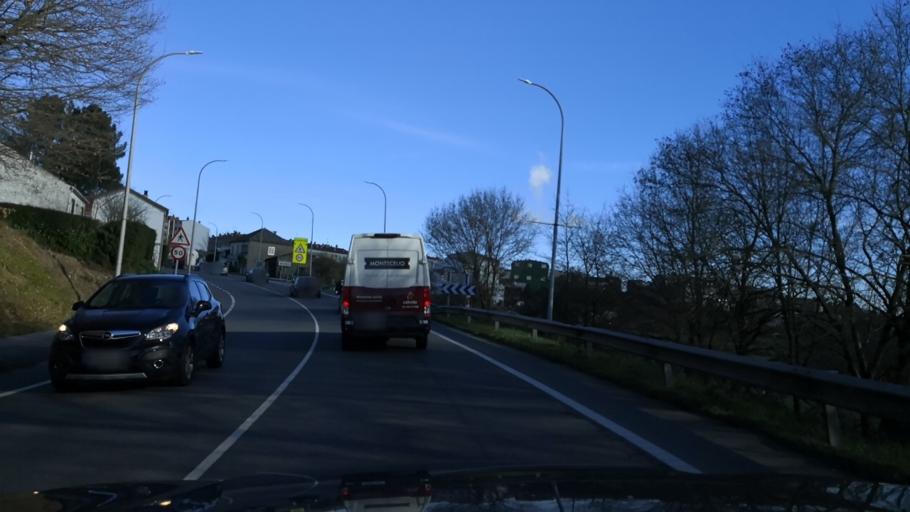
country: ES
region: Galicia
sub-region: Provincia de Pontevedra
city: Silleda
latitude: 42.6994
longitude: -8.2532
